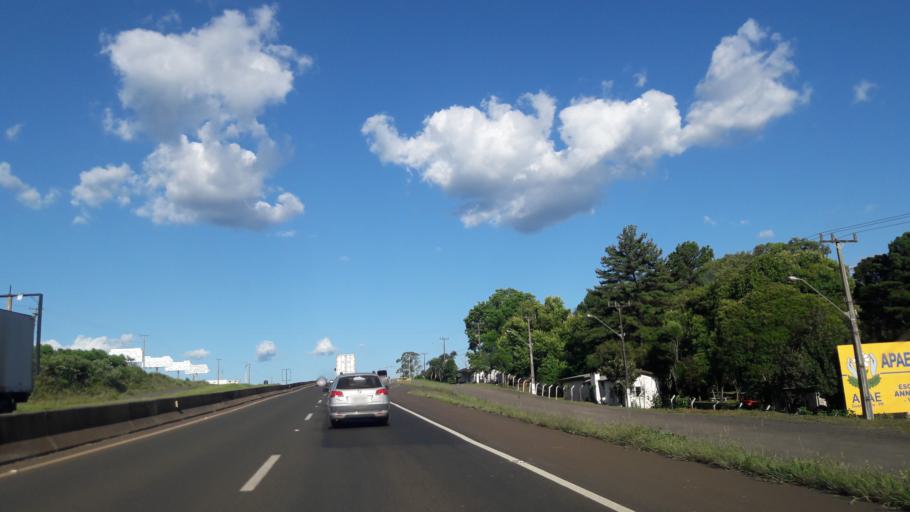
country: BR
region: Parana
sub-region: Guarapuava
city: Guarapuava
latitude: -25.3473
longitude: -51.4509
